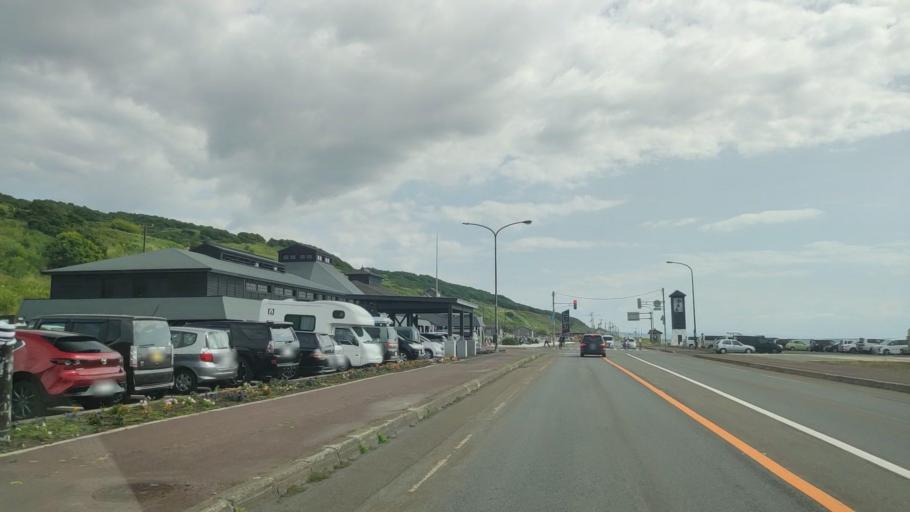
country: JP
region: Hokkaido
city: Rumoi
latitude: 44.1379
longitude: 141.6546
